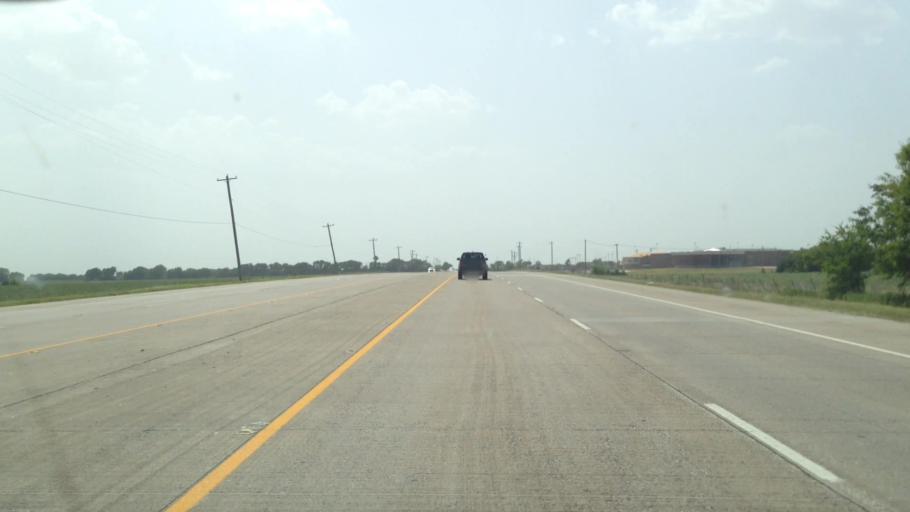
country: US
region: Texas
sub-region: Collin County
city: Princeton
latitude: 33.1714
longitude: -96.4787
